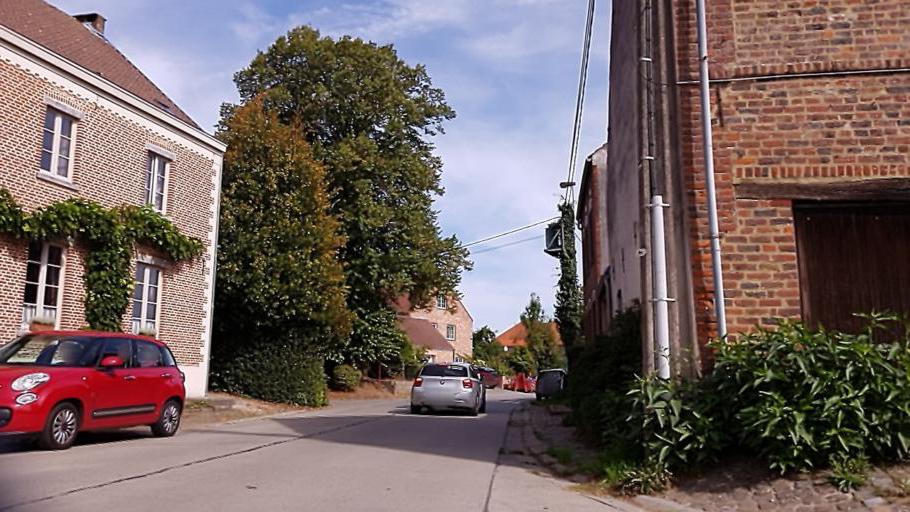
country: BE
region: Wallonia
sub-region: Province du Brabant Wallon
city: Grez-Doiceau
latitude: 50.7628
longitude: 4.6961
